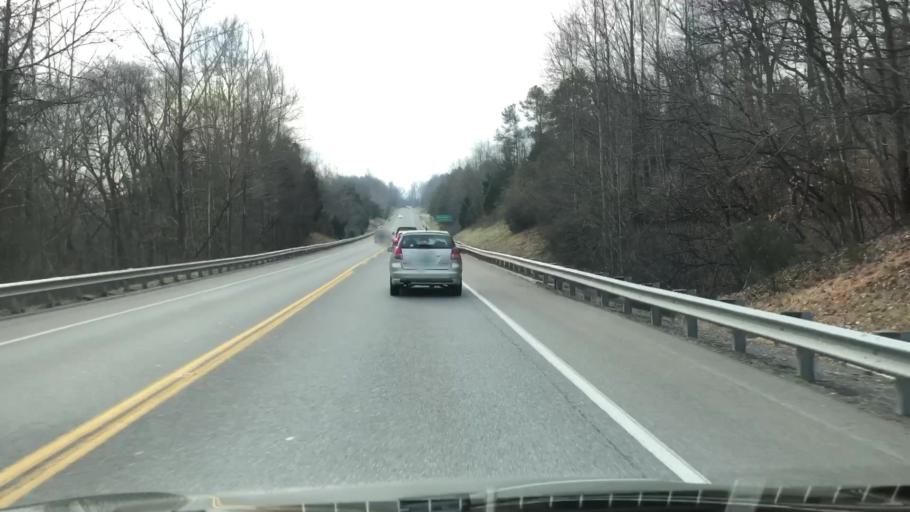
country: US
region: Virginia
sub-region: City of Lynchburg
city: West Lynchburg
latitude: 37.4289
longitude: -79.2349
